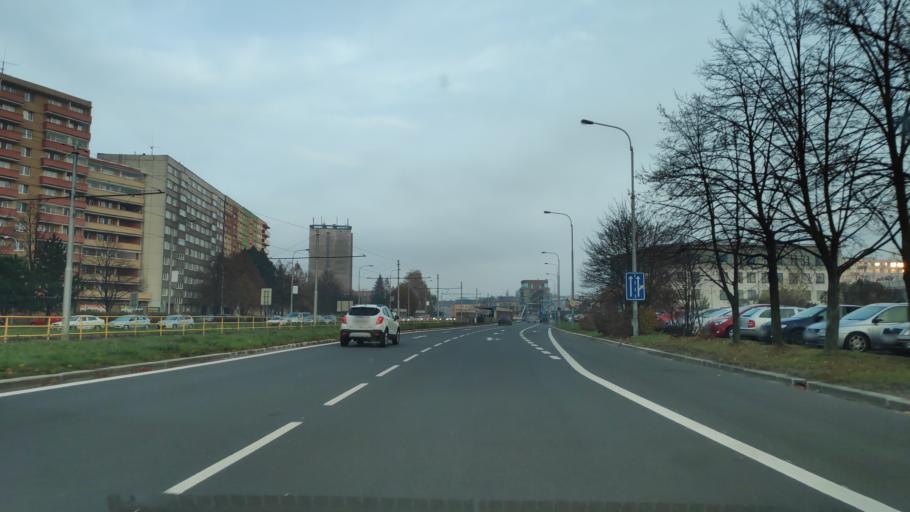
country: CZ
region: Moravskoslezsky
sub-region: Okres Ostrava-Mesto
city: Ostrava
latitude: 49.7852
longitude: 18.2565
